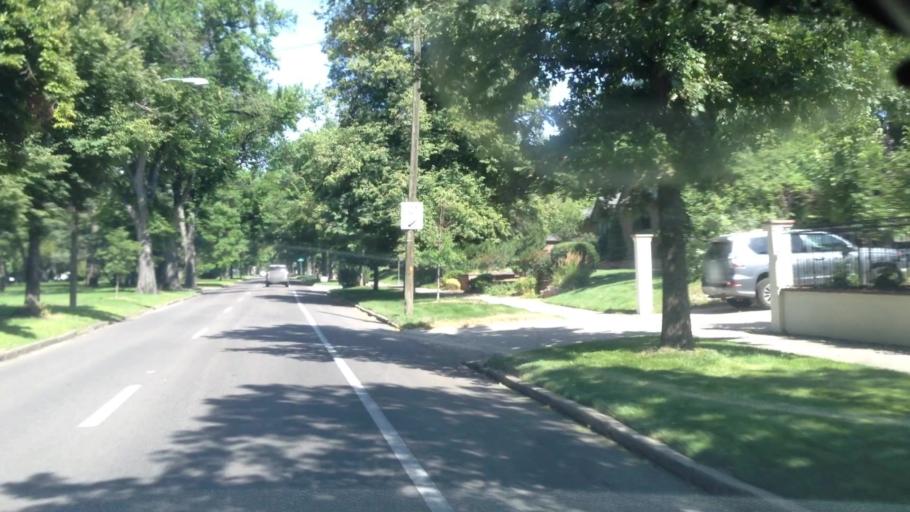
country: US
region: Colorado
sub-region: Arapahoe County
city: Glendale
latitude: 39.7434
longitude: -104.9198
